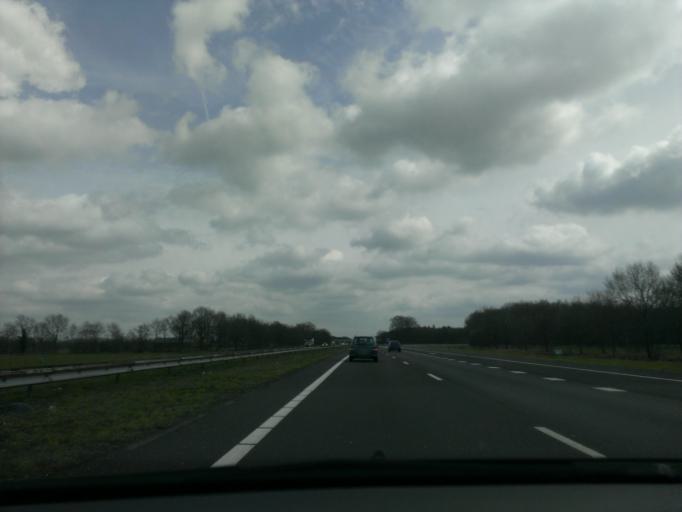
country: NL
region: Gelderland
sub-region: Gemeente Lochem
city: Harfsen
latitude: 52.2431
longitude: 6.2977
